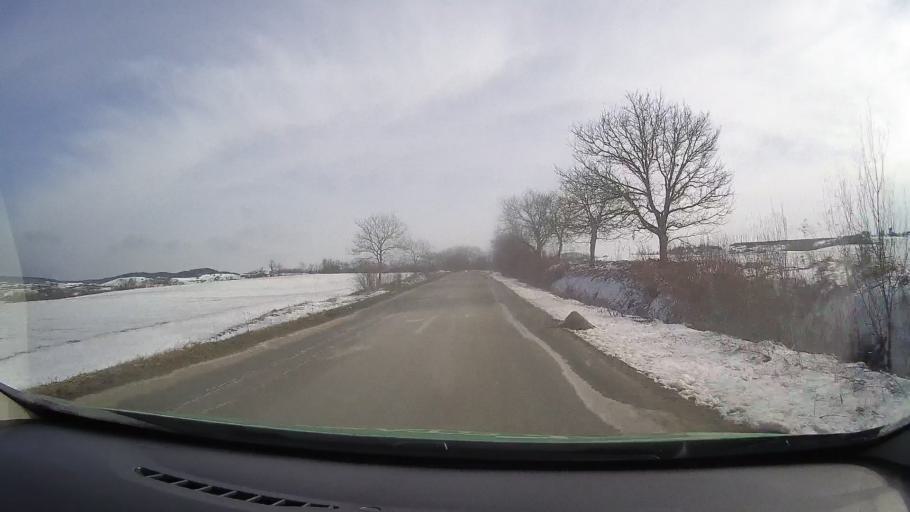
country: RO
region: Mures
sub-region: Comuna Apold
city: Apold
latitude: 46.1156
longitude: 24.8262
